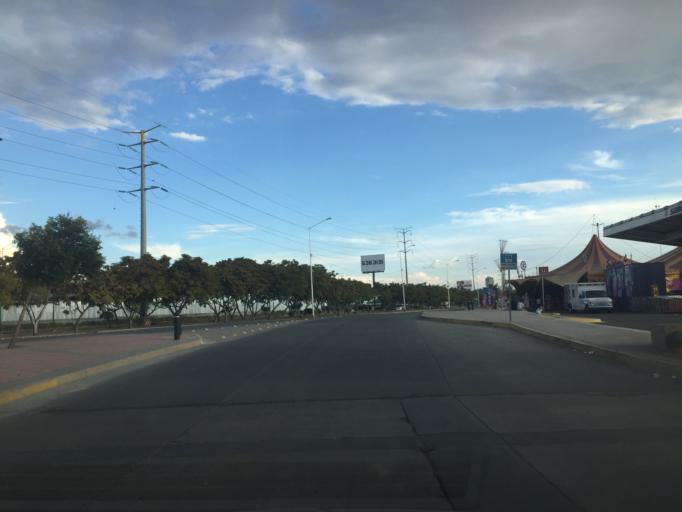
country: MX
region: Guanajuato
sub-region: Leon
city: Medina
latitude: 21.1408
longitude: -101.6331
